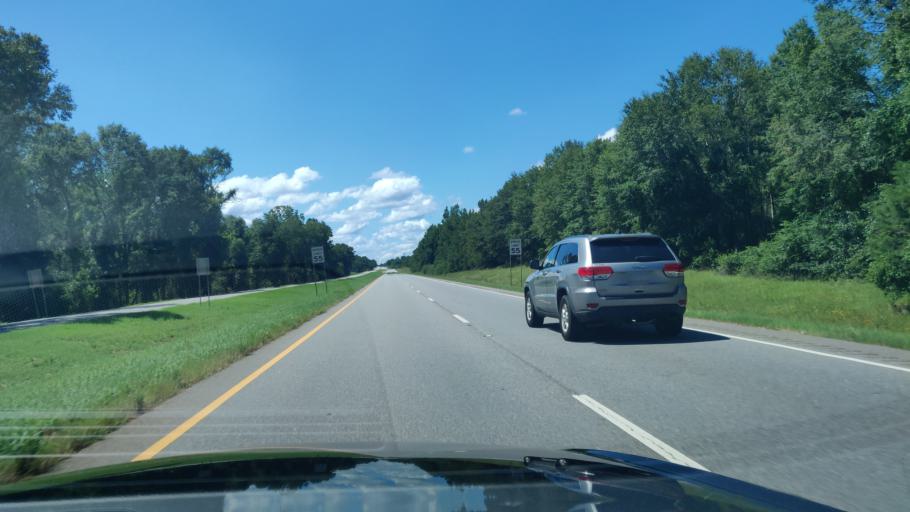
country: US
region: Georgia
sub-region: Terrell County
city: Dawson
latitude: 31.8799
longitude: -84.5005
